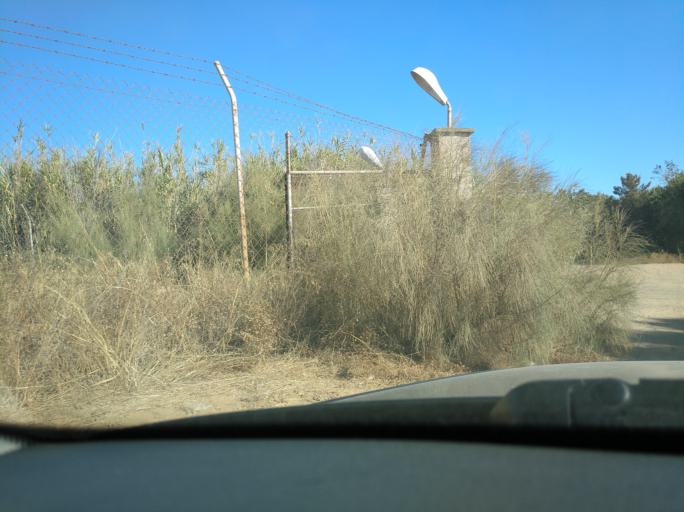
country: PT
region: Faro
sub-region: Vila Real de Santo Antonio
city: Monte Gordo
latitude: 37.1700
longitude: -7.5068
